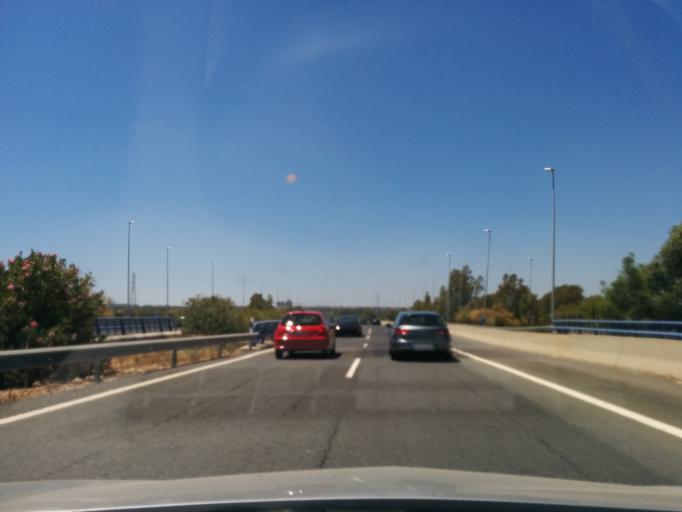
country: ES
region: Andalusia
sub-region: Provincia de Huelva
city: Gibraleon
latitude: 37.3565
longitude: -6.9589
